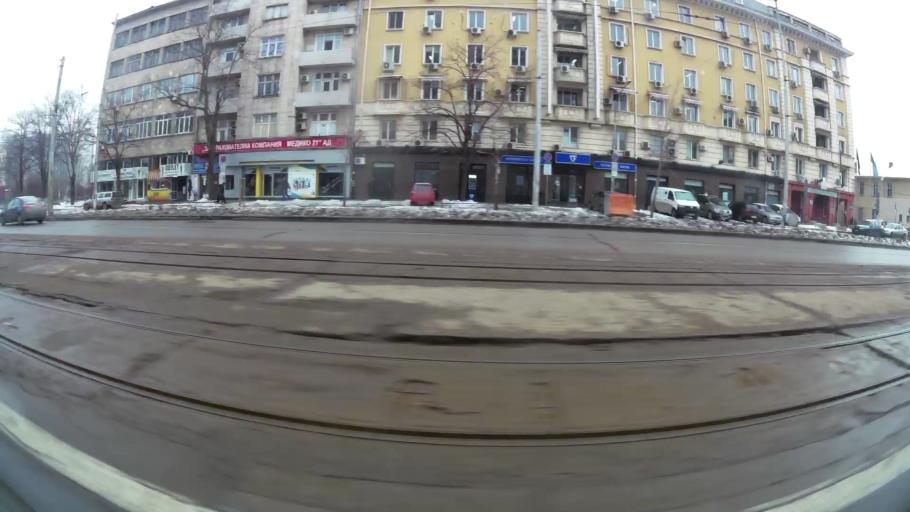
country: BG
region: Sofia-Capital
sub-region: Stolichna Obshtina
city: Sofia
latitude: 42.7086
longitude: 23.3227
